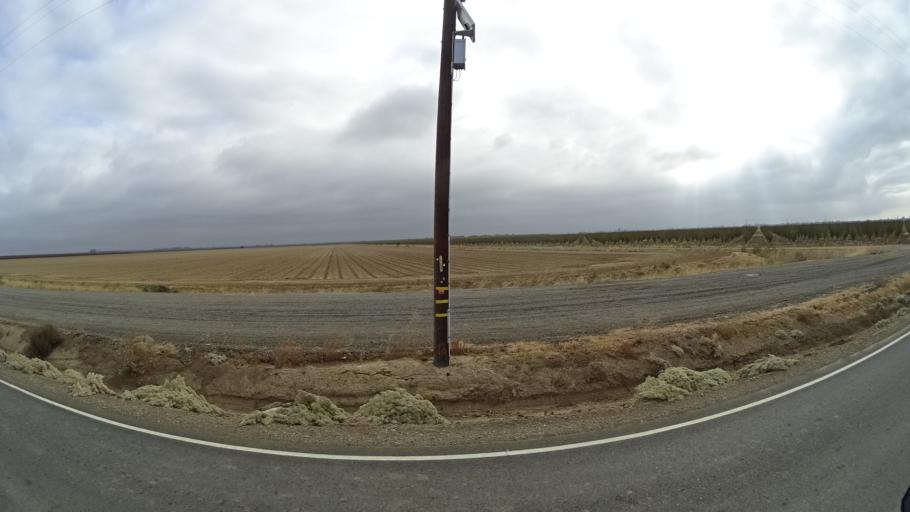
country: US
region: California
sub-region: Yolo County
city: Esparto
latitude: 38.7243
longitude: -122.0464
